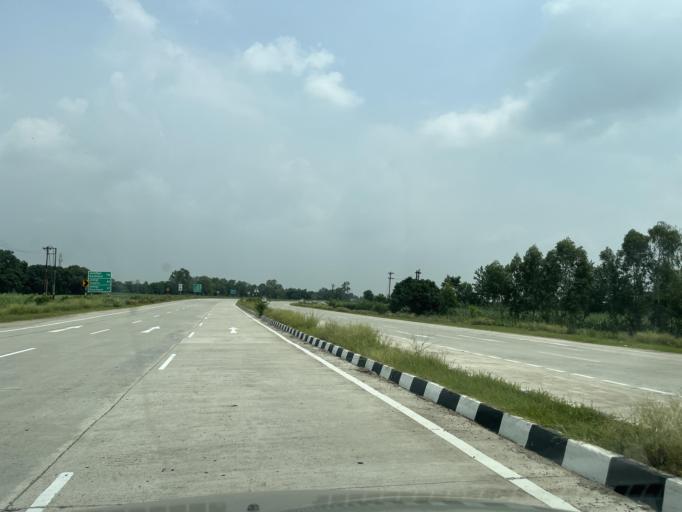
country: IN
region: Uttar Pradesh
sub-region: Bijnor
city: Nagina
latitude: 29.4253
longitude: 78.4391
